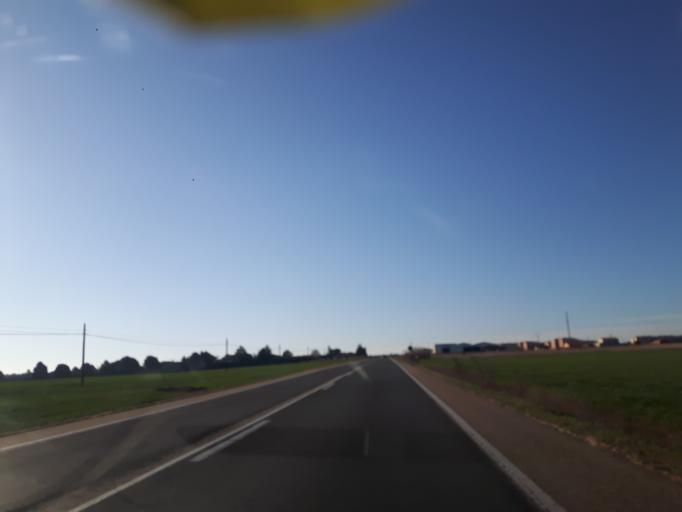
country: ES
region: Castille and Leon
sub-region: Provincia de Salamanca
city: Calvarrasa de Arriba
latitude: 40.8919
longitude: -5.5853
